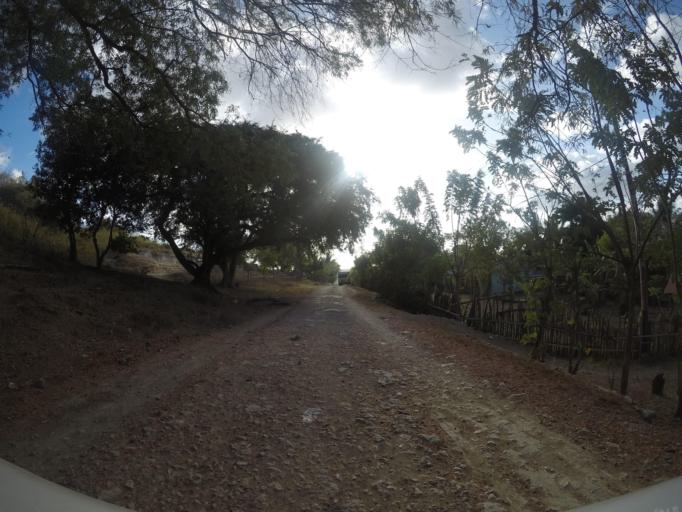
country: TL
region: Lautem
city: Lospalos
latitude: -8.4296
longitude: 126.8465
